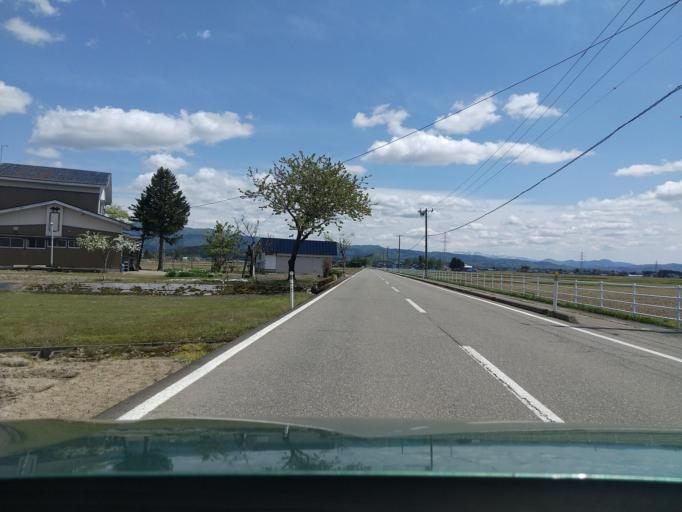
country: JP
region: Akita
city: Omagari
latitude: 39.3869
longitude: 140.5102
